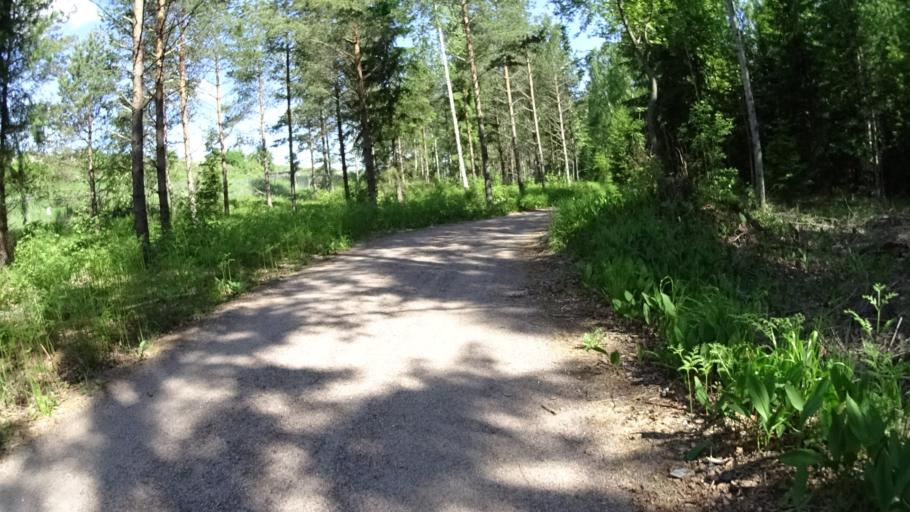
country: FI
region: Uusimaa
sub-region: Helsinki
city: Kilo
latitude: 60.3041
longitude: 24.8104
